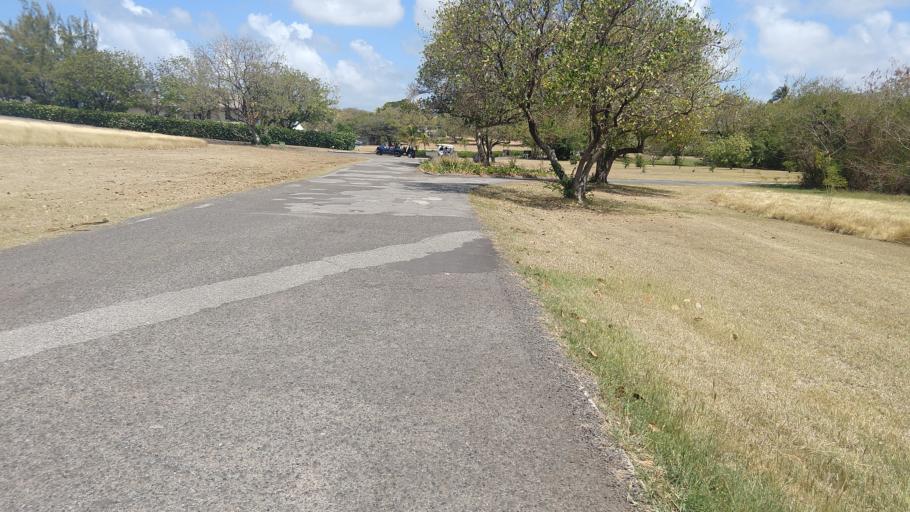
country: VC
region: Grenadines
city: Port Elizabeth
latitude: 12.8883
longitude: -61.1845
